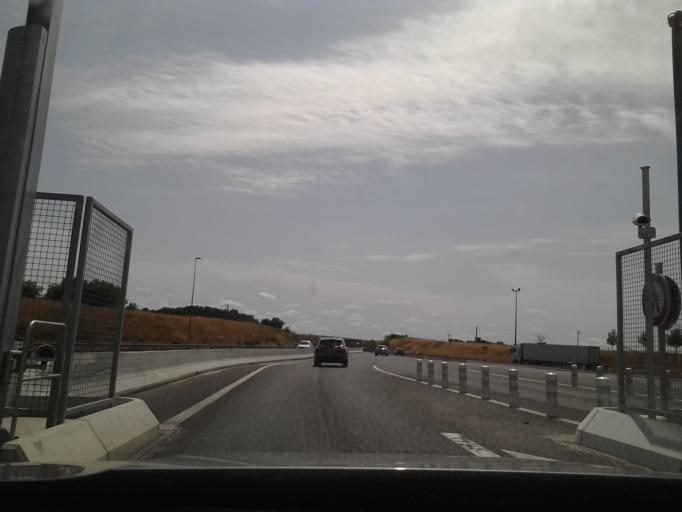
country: FR
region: Centre
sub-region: Departement d'Indre-et-Loire
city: Saint-Christophe-sur-le-Nais
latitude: 47.6382
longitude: 0.4970
